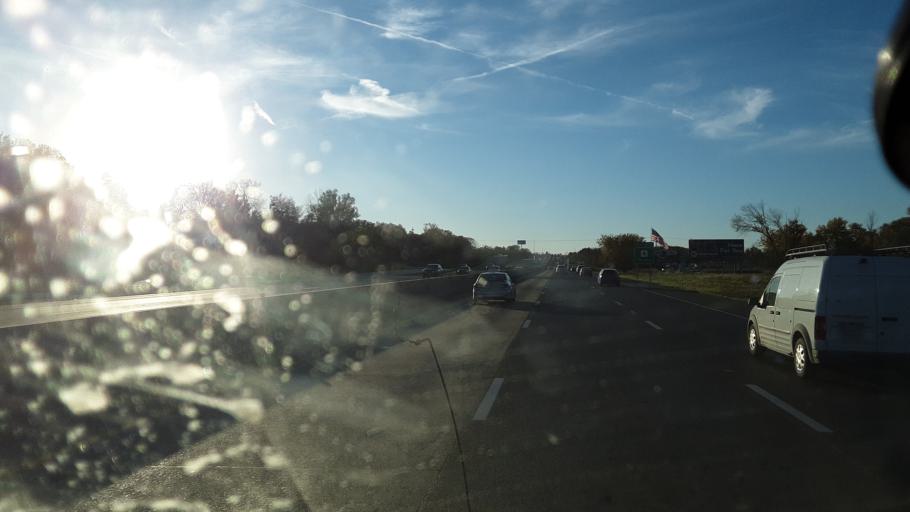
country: US
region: Missouri
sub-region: Saint Charles County
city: Lake Saint Louis
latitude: 38.8053
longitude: -90.7968
